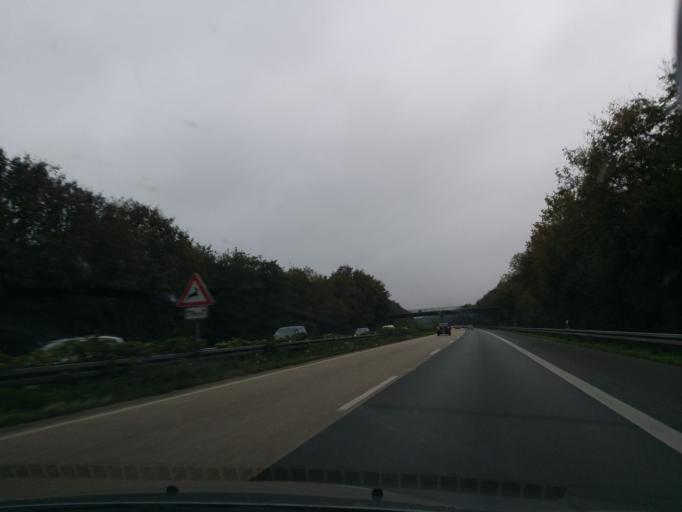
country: DE
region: North Rhine-Westphalia
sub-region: Regierungsbezirk Munster
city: Senden
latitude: 51.8637
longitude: 7.5760
